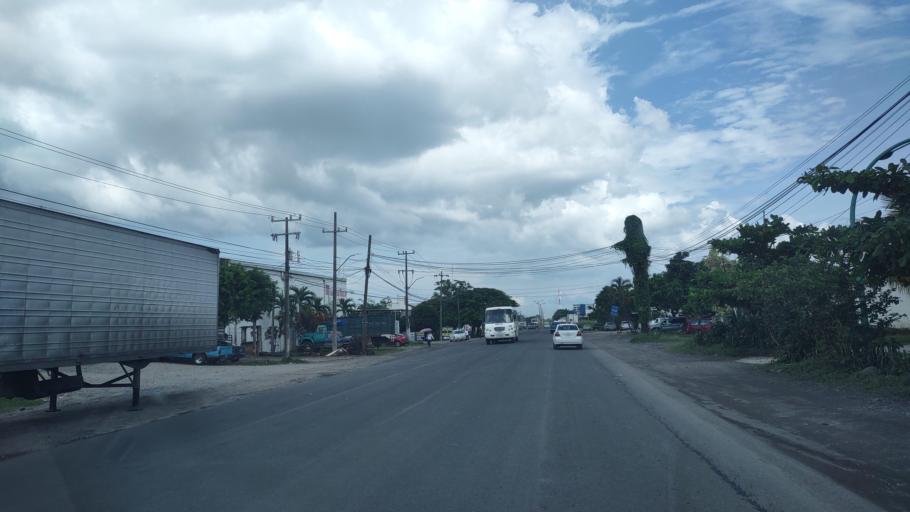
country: MX
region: Veracruz
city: Martinez de la Torre
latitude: 20.0687
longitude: -97.0727
